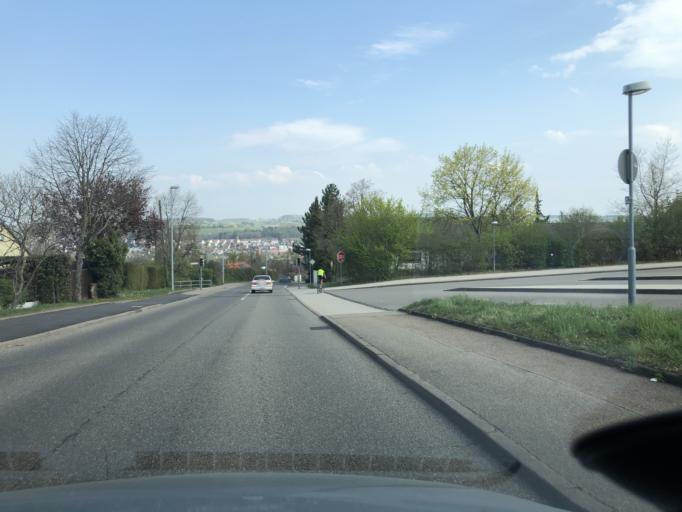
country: DE
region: Baden-Wuerttemberg
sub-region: Regierungsbezirk Stuttgart
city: Weil der Stadt
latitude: 48.7528
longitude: 8.8614
